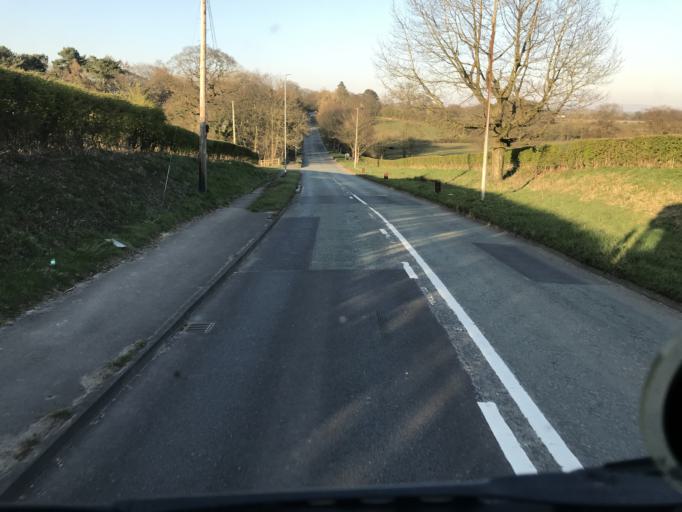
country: GB
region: England
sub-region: Cheshire East
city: Mottram St. Andrew
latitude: 53.3321
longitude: -2.1876
